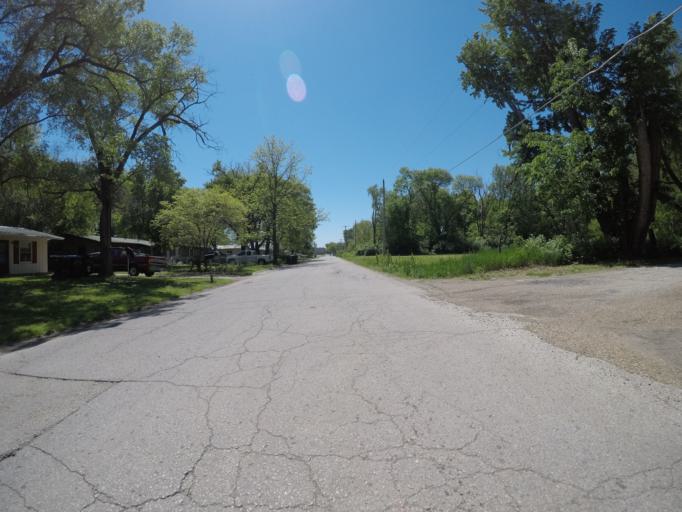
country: US
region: Kansas
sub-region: Shawnee County
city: Topeka
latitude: 39.0485
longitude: -95.6367
